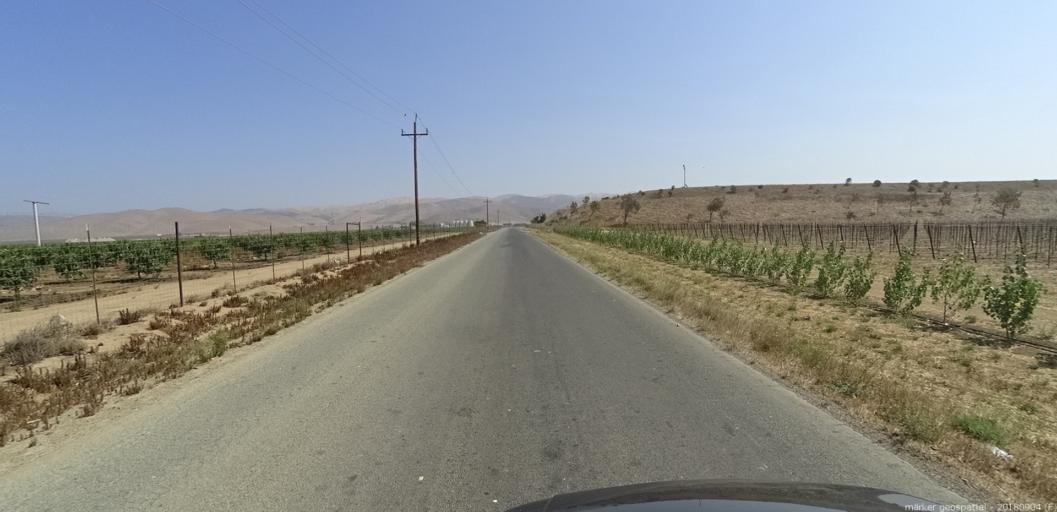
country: US
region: California
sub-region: Monterey County
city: Gonzales
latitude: 36.5295
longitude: -121.4137
